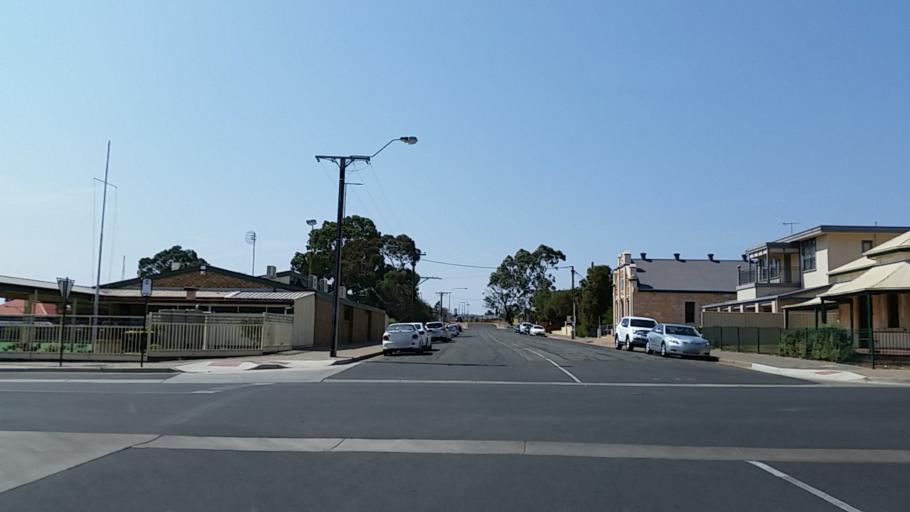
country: AU
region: South Australia
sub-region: Port Augusta
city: Port Augusta West
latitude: -32.4919
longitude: 137.7642
